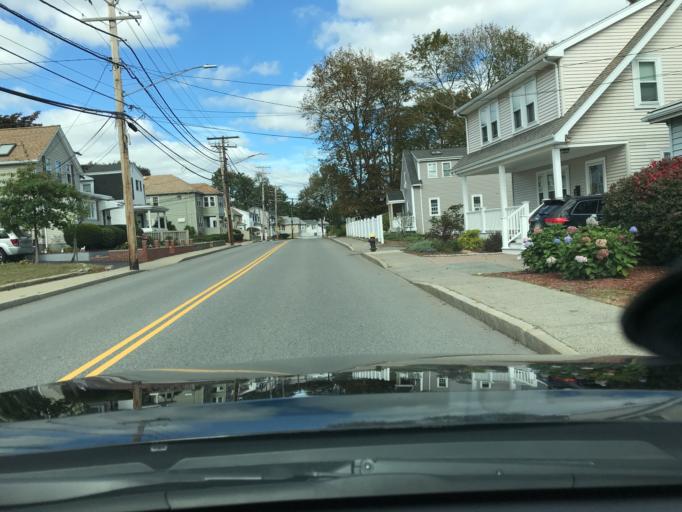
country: US
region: Massachusetts
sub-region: Norfolk County
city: Dedham
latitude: 42.2807
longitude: -71.1681
